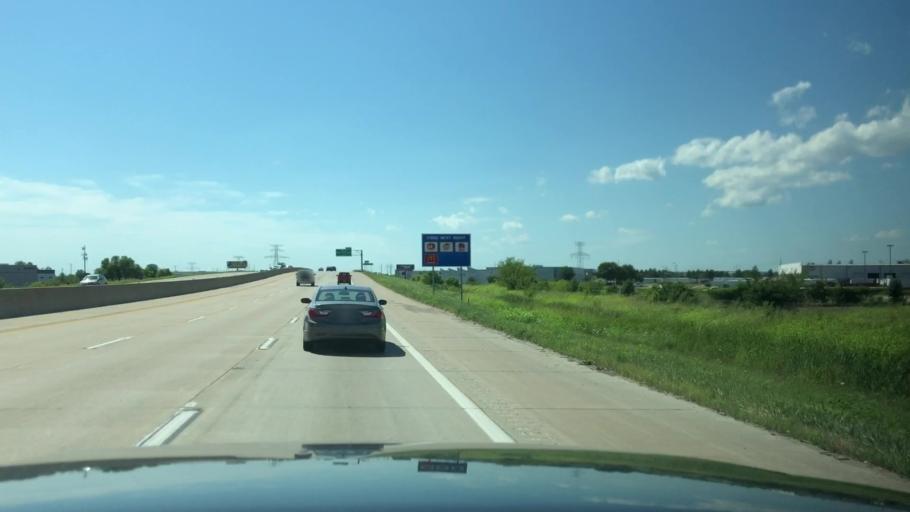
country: US
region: Missouri
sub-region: Saint Charles County
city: Saint Charles
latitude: 38.8207
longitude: -90.5034
